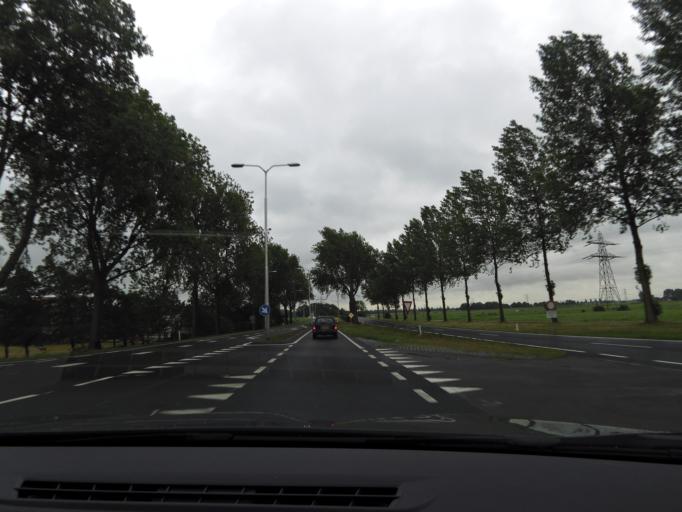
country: NL
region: South Holland
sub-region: Gemeente Maassluis
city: Maassluis
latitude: 51.8653
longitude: 4.2273
